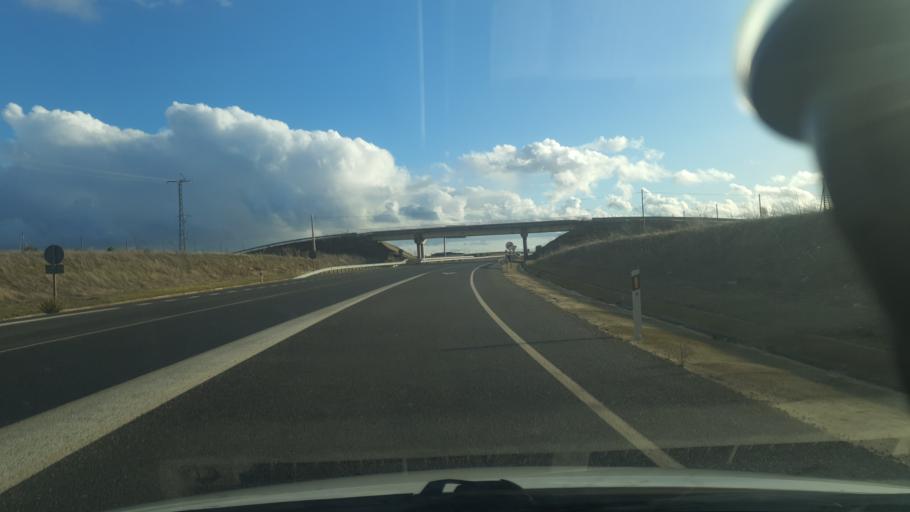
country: ES
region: Castille and Leon
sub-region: Provincia de Segovia
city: San Cristobal de la Vega
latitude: 41.1117
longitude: -4.6376
